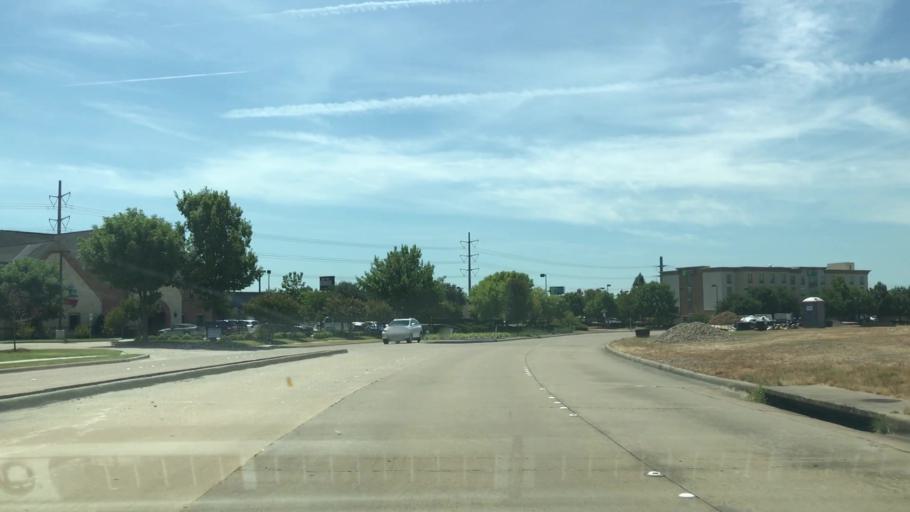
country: US
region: Texas
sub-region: Collin County
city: Allen
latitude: 33.1077
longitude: -96.6780
